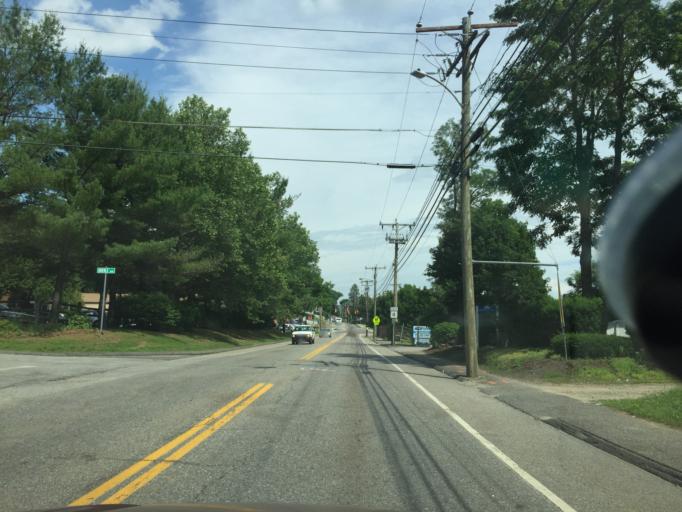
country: US
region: Connecticut
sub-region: Litchfield County
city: West Torrington
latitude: 41.8140
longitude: -73.1356
